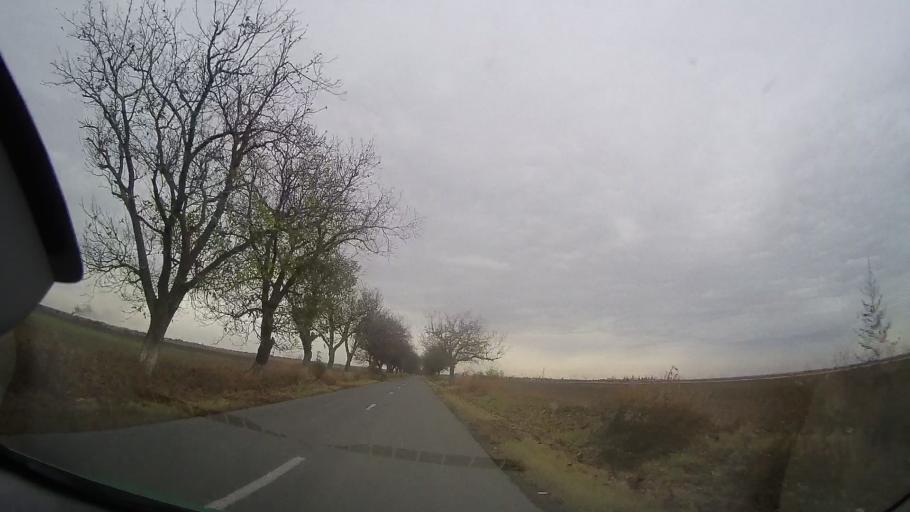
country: RO
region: Prahova
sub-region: Comuna Fantanele
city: Fantanele
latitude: 45.0131
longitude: 26.4097
